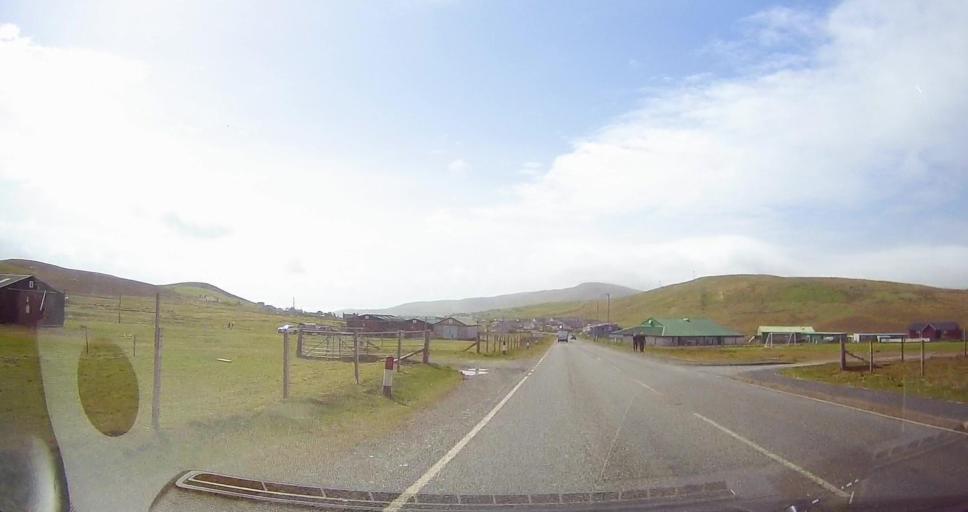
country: GB
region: Scotland
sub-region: Shetland Islands
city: Sandwick
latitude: 60.0596
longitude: -1.2220
